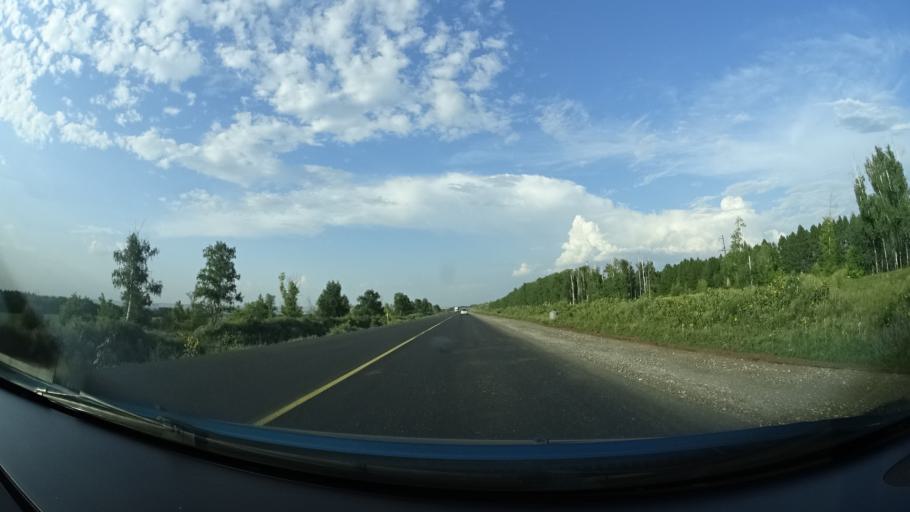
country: RU
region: Samara
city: Sukhodol
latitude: 53.7547
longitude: 50.8732
